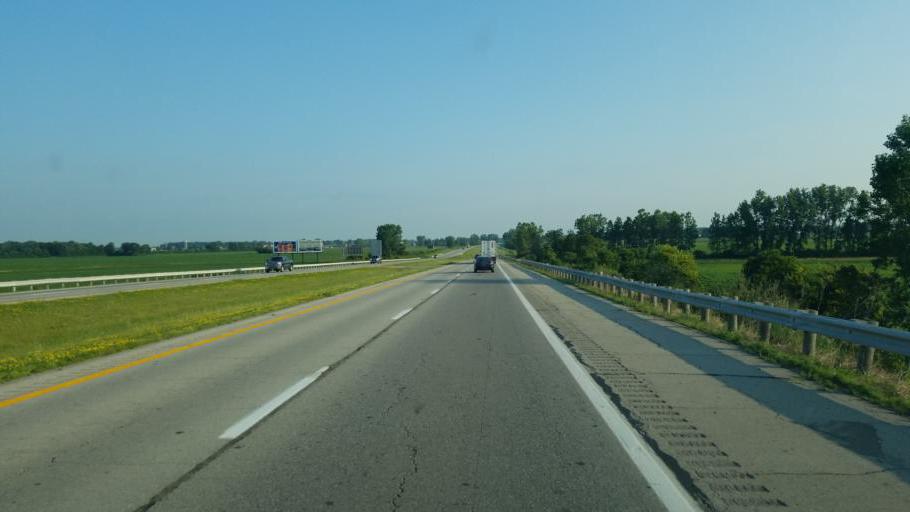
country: US
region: Ohio
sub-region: Marion County
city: Marion
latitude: 40.6023
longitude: -83.0878
